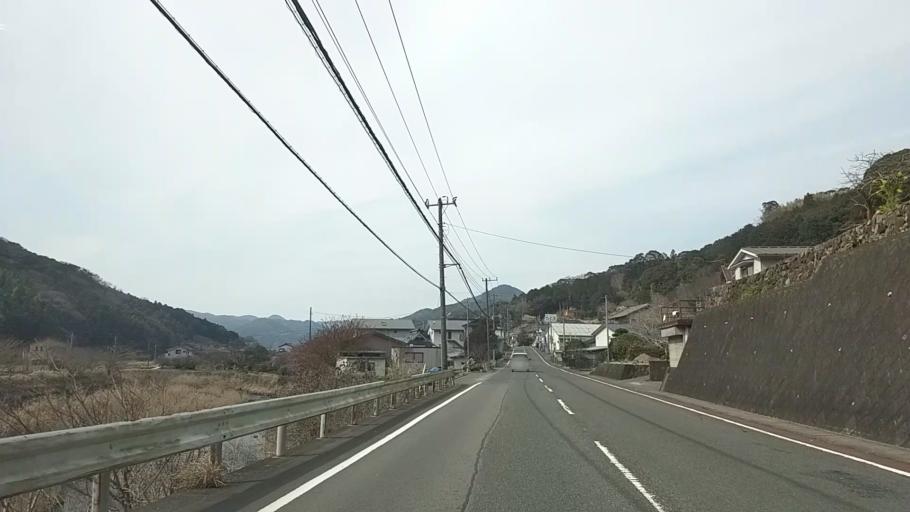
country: JP
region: Shizuoka
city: Shimoda
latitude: 34.7227
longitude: 138.9415
